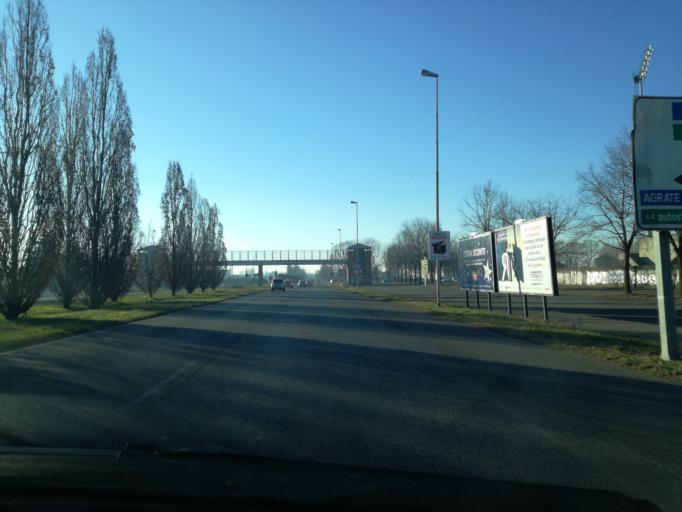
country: IT
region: Lombardy
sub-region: Provincia di Monza e Brianza
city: Villasanta
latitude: 45.5833
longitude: 9.3099
